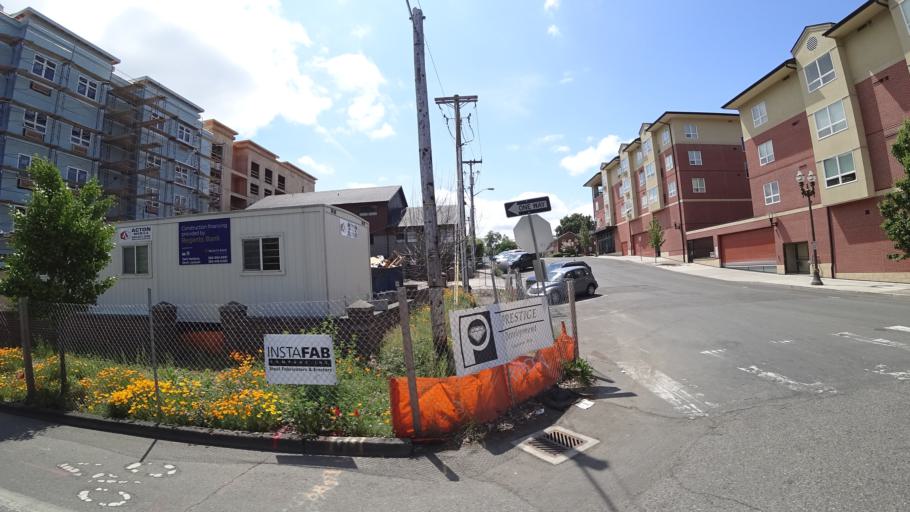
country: US
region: Washington
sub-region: Clark County
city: Vancouver
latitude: 45.6318
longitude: -122.6683
